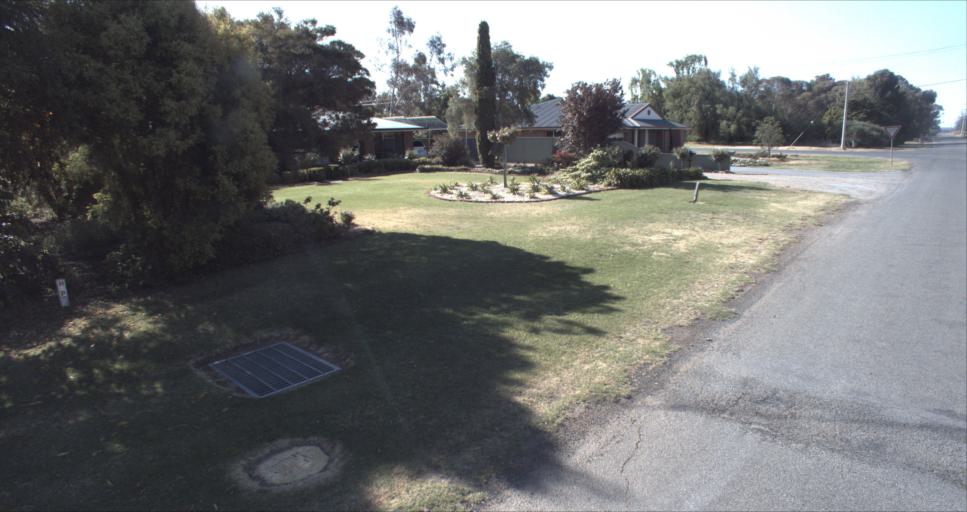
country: AU
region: New South Wales
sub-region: Leeton
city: Leeton
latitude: -34.5441
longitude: 146.4150
